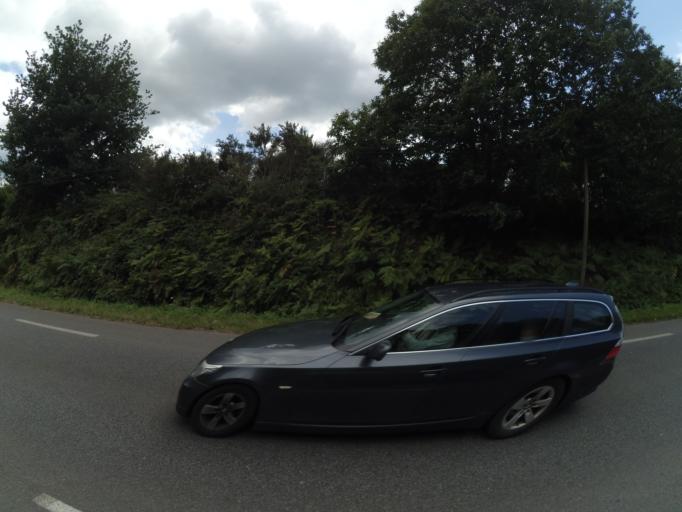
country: FR
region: Brittany
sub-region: Departement du Morbihan
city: Hennebont
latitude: 47.7613
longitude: -3.2909
